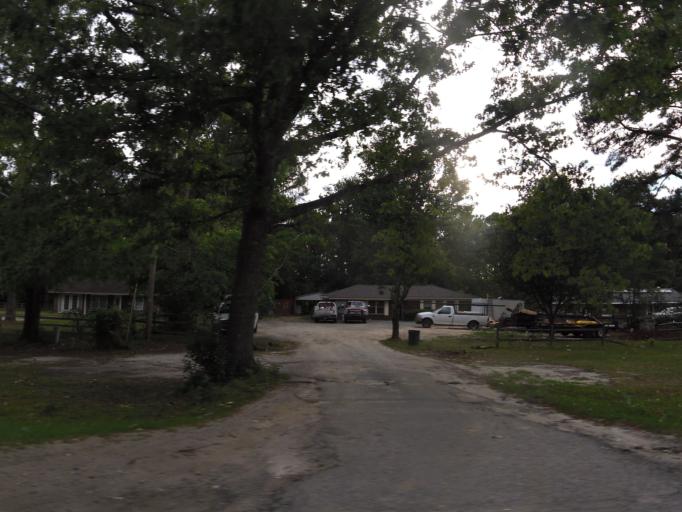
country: US
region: South Carolina
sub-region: Jasper County
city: Hardeeville
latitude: 32.3131
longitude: -81.0883
